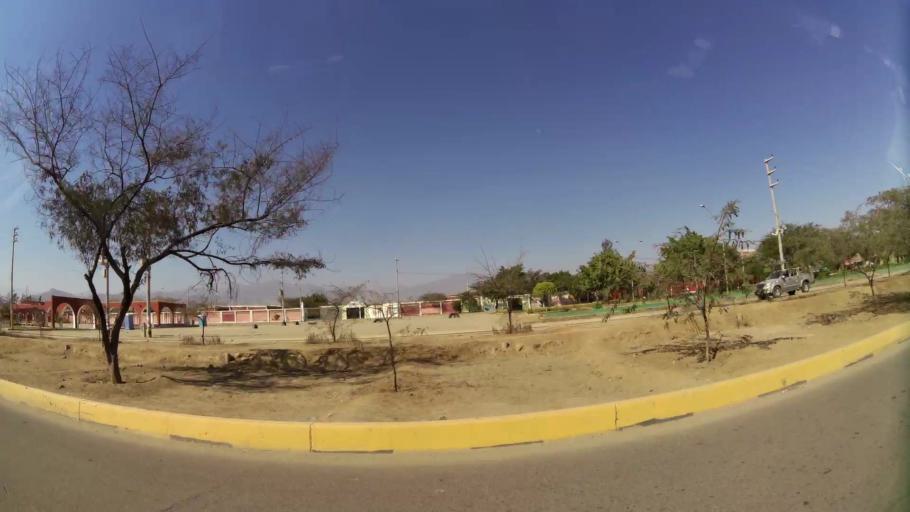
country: PE
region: Ica
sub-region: Provincia de Ica
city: La Tinguina
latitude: -14.0330
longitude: -75.7074
